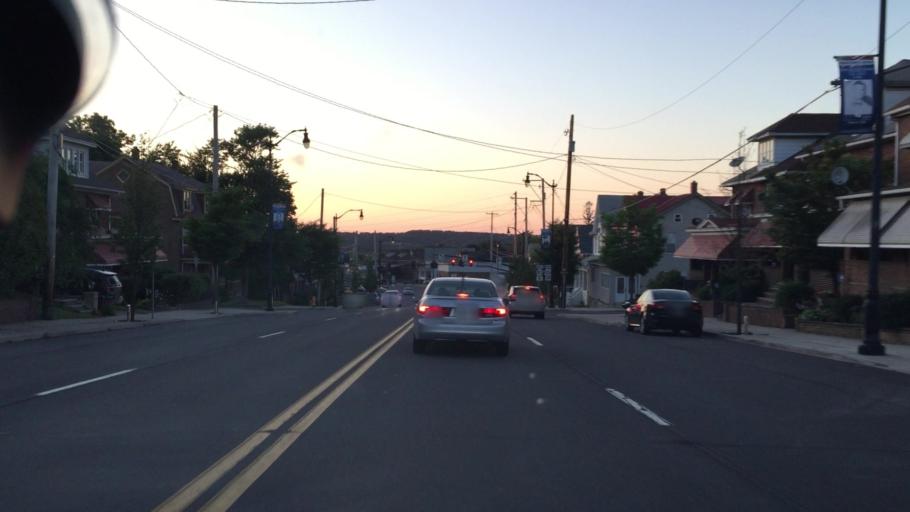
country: US
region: Pennsylvania
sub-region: Luzerne County
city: West Hazleton
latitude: 40.9634
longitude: -75.9968
